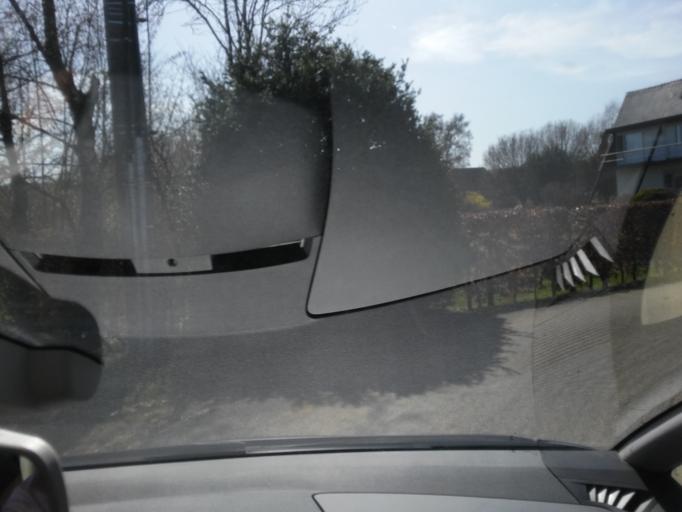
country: BE
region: Wallonia
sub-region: Province du Luxembourg
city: Daverdisse
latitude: 50.0203
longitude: 5.1211
